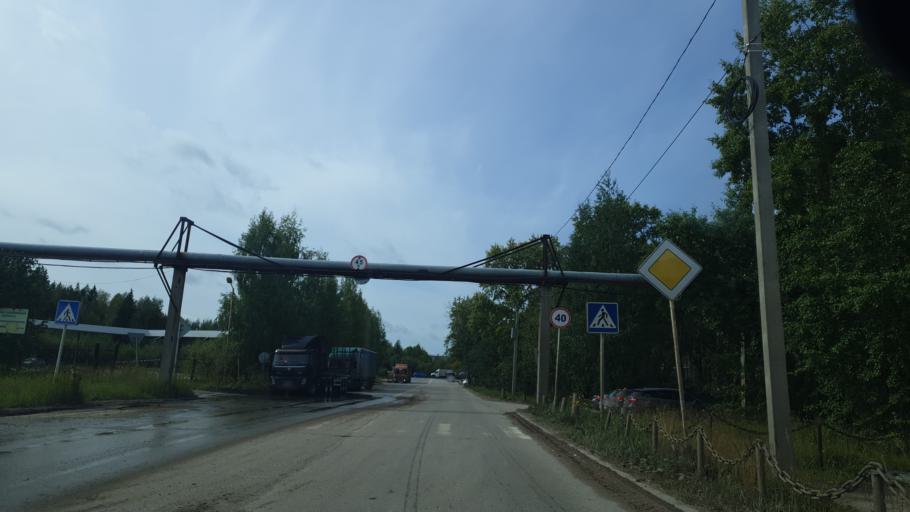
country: RU
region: Komi Republic
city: Ezhva
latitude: 61.8083
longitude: 50.7306
